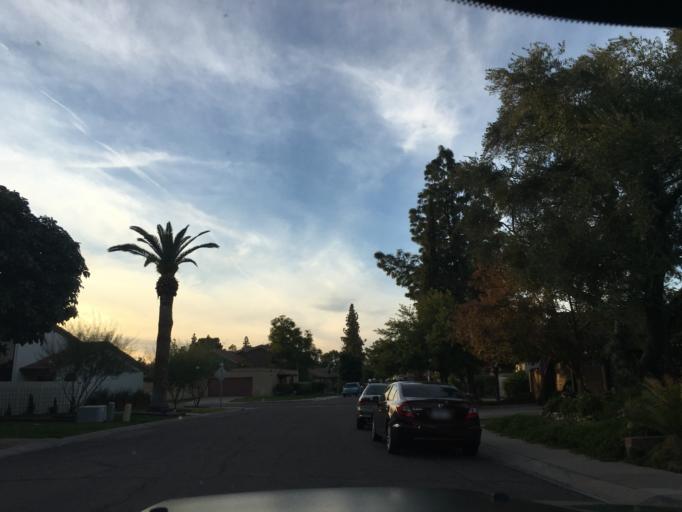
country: US
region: Arizona
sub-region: Maricopa County
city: Tempe
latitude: 33.3748
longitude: -111.9167
